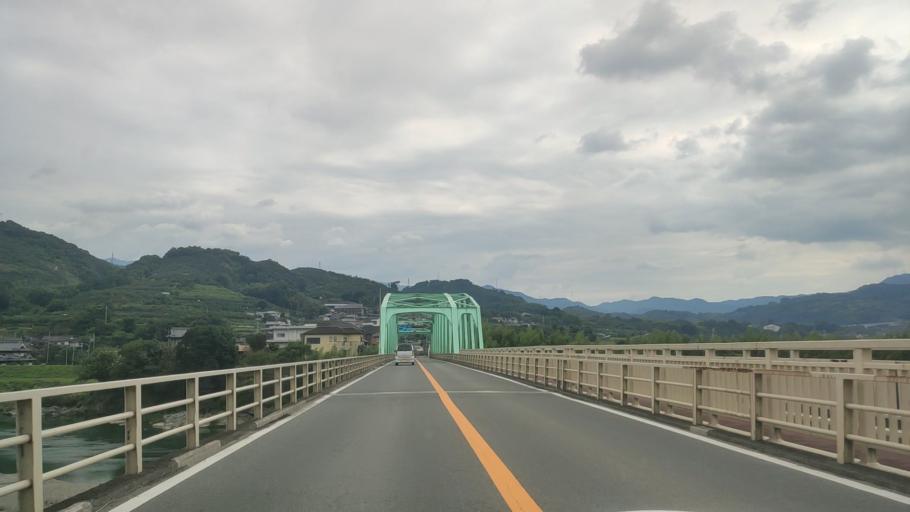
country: JP
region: Wakayama
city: Hashimoto
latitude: 34.2992
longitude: 135.5783
